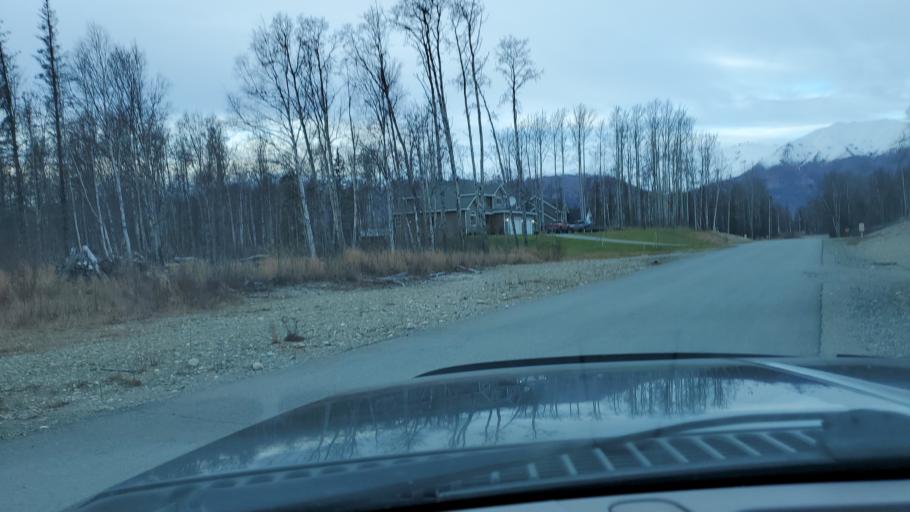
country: US
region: Alaska
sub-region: Matanuska-Susitna Borough
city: Lakes
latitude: 61.6554
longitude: -149.3035
